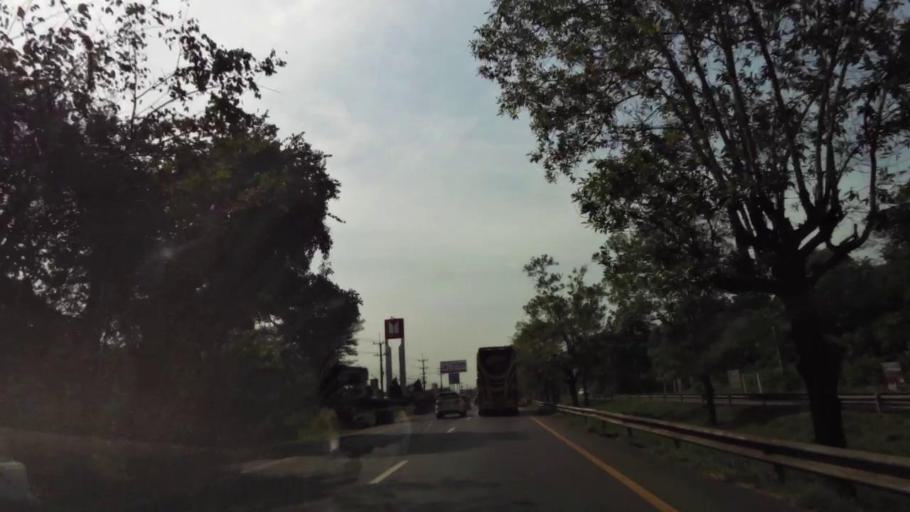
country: TH
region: Chanthaburi
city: Chanthaburi
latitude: 12.6636
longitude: 102.0813
